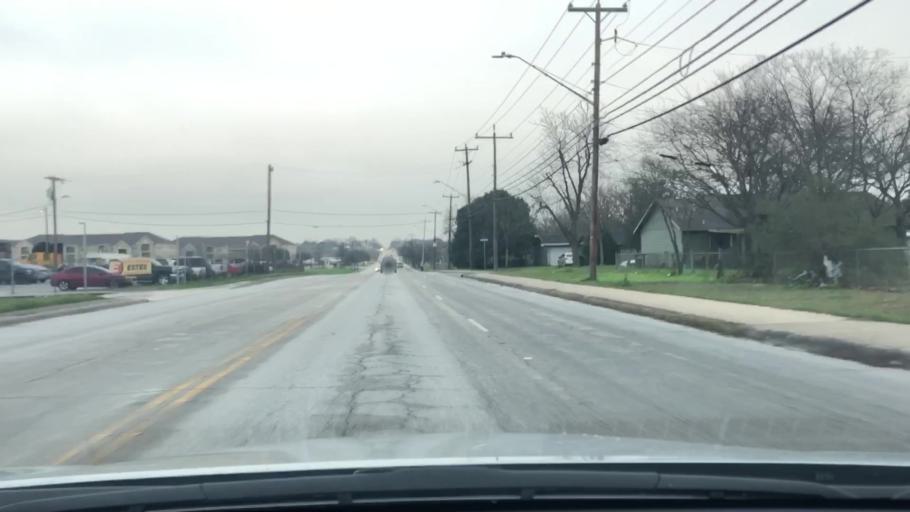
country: US
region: Texas
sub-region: Bexar County
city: Terrell Hills
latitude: 29.4355
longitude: -98.4272
